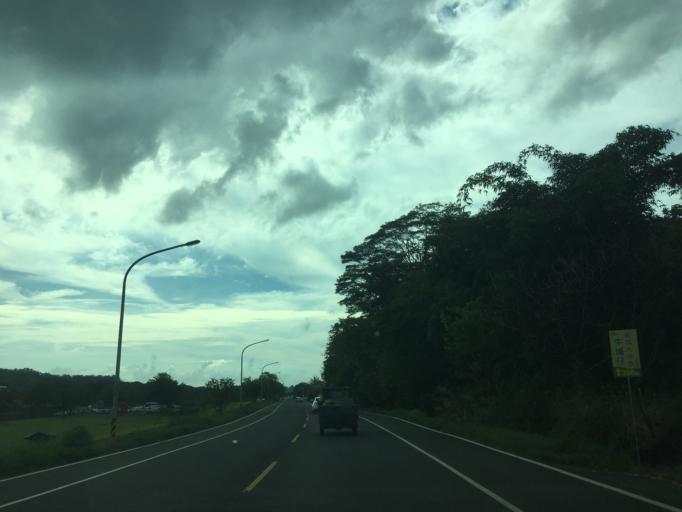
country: TW
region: Taiwan
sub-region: Chiayi
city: Jiayi Shi
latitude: 23.4426
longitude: 120.5942
